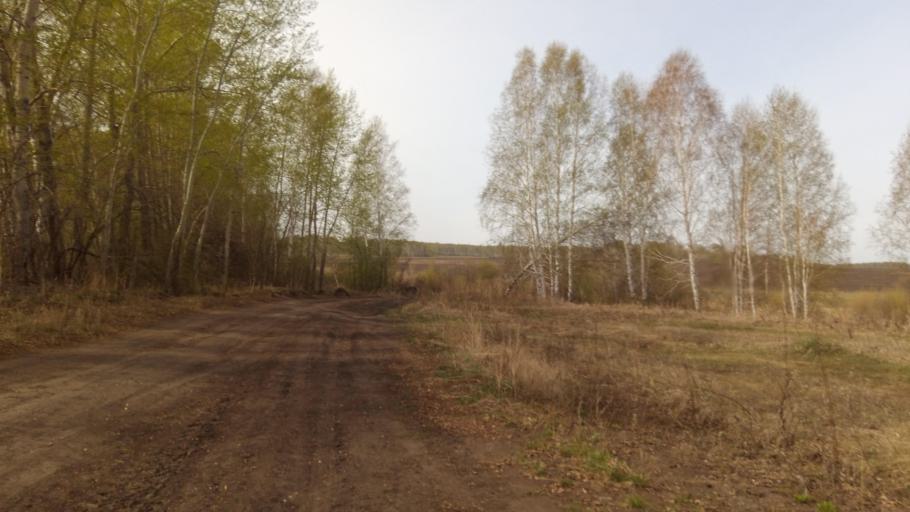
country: RU
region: Chelyabinsk
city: Timiryazevskiy
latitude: 55.0264
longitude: 60.8564
